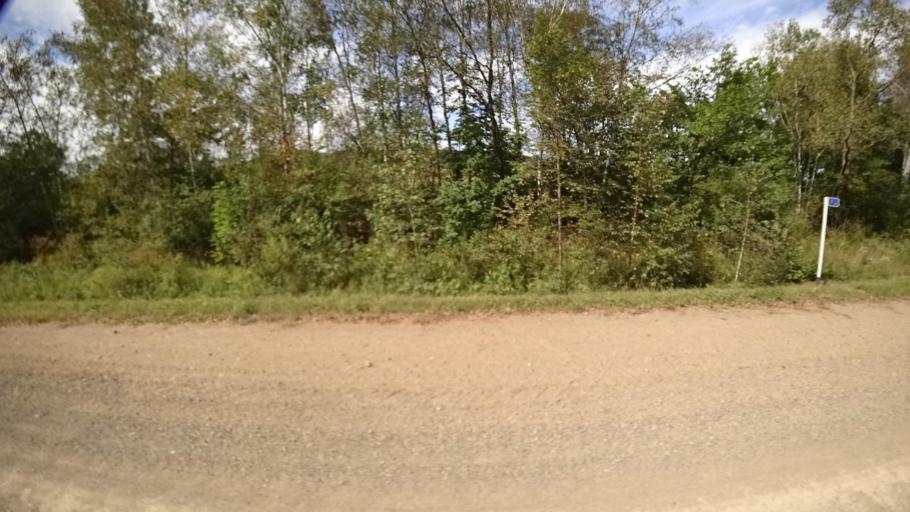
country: RU
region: Primorskiy
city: Yakovlevka
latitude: 44.6954
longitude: 133.6201
